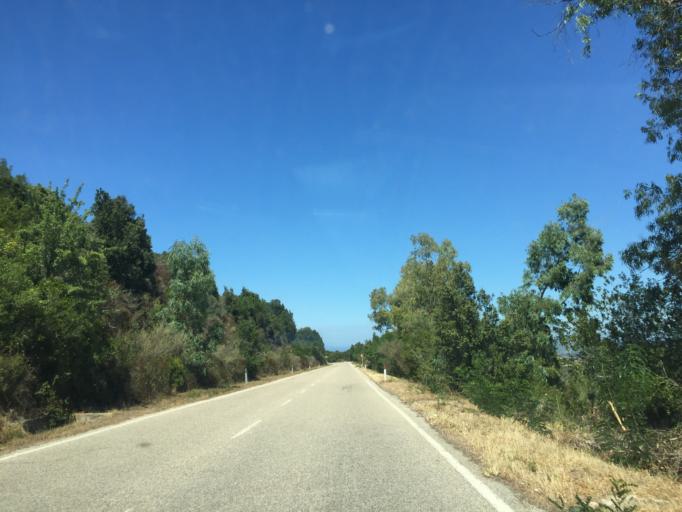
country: IT
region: Sardinia
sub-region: Provincia di Olbia-Tempio
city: Aglientu
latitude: 41.0858
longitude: 9.1177
